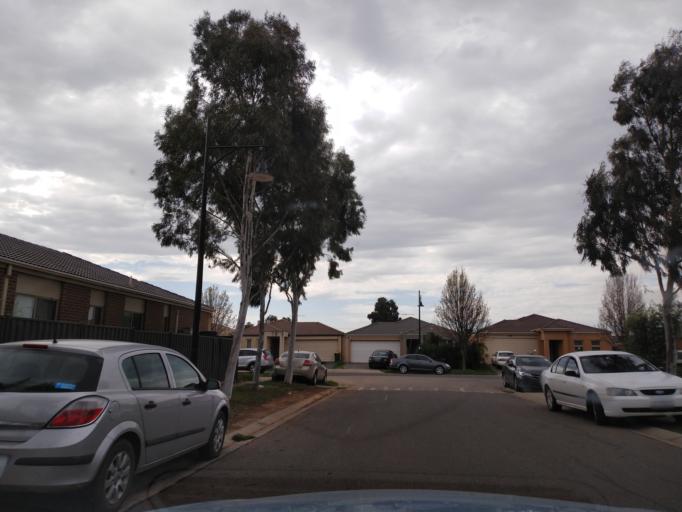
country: AU
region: Victoria
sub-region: Wyndham
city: Williams Landing
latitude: -37.8389
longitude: 144.7158
